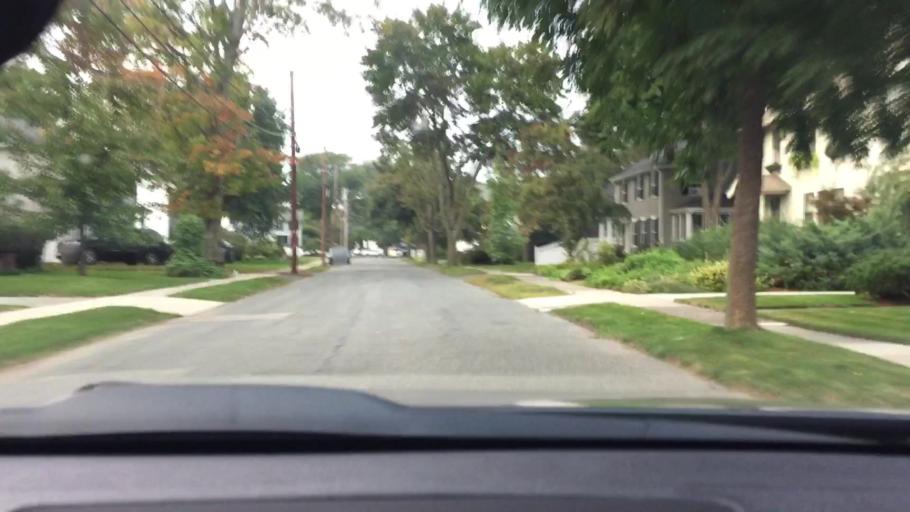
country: US
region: Massachusetts
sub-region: Norfolk County
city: Needham
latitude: 42.2787
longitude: -71.2250
